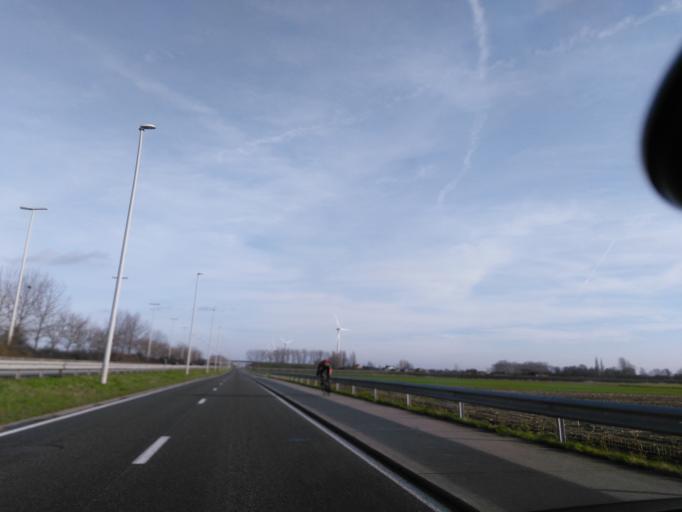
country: BE
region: Flanders
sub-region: Provincie Oost-Vlaanderen
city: Sint-Gillis-Waas
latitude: 51.2325
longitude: 4.1362
